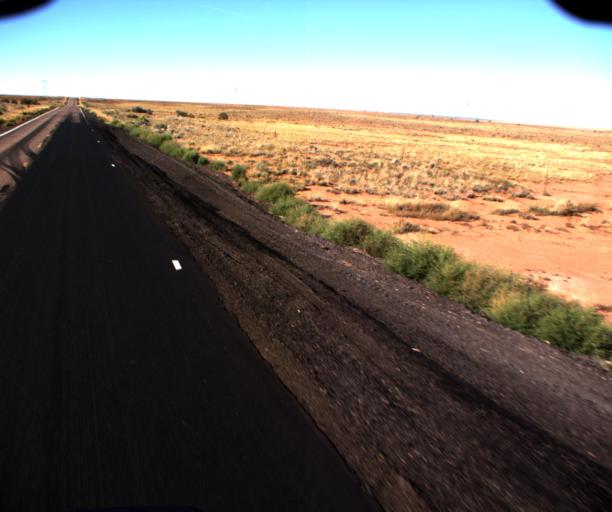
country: US
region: Arizona
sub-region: Navajo County
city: Holbrook
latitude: 34.8048
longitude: -110.2070
